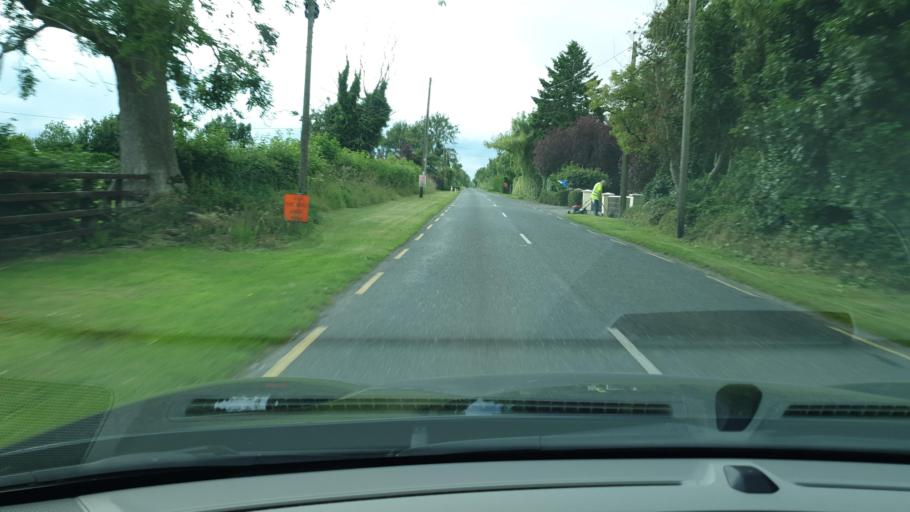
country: IE
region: Leinster
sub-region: An Mhi
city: Ratoath
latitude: 53.5332
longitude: -6.4925
